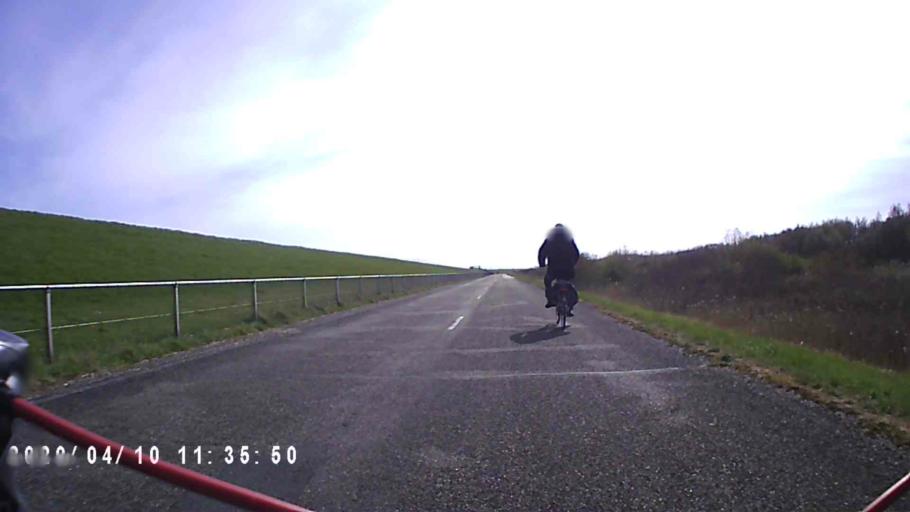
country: NL
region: Groningen
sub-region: Gemeente De Marne
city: Ulrum
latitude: 53.4041
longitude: 6.2868
